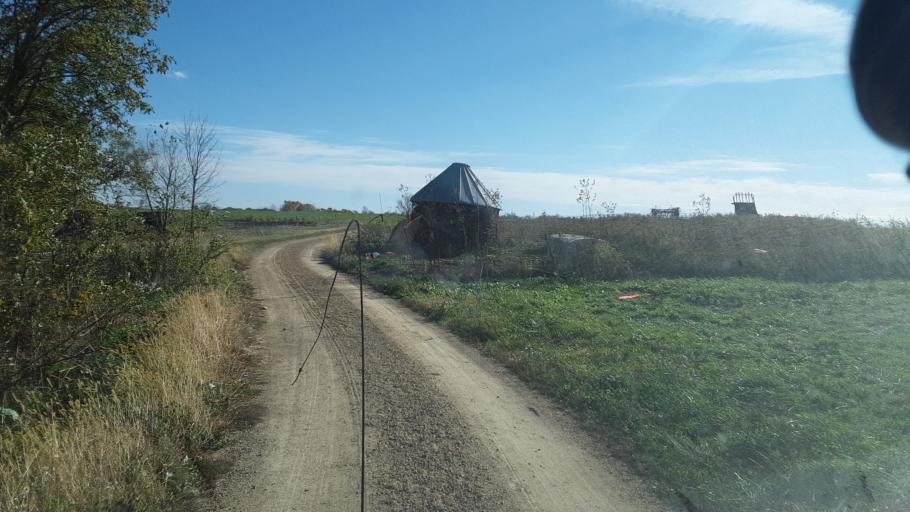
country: US
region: Wisconsin
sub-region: Vernon County
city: Hillsboro
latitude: 43.6857
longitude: -90.4097
